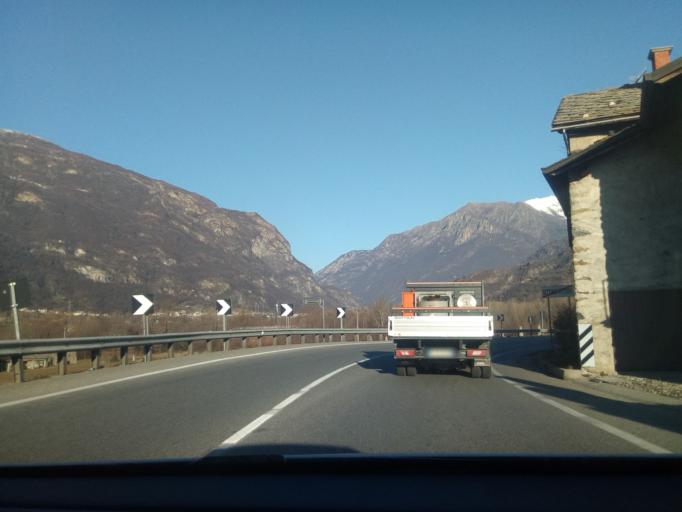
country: IT
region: Piedmont
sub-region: Provincia di Torino
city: Settimo Vittone
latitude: 45.5516
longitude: 7.8271
